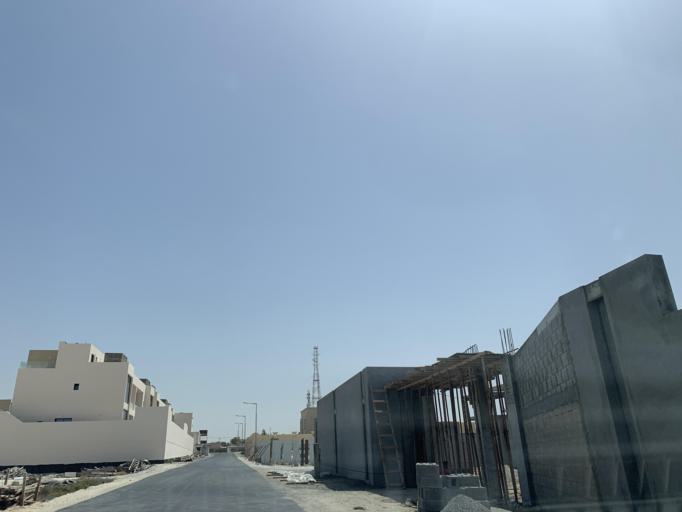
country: BH
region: Northern
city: Ar Rifa'
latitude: 26.1485
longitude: 50.5459
